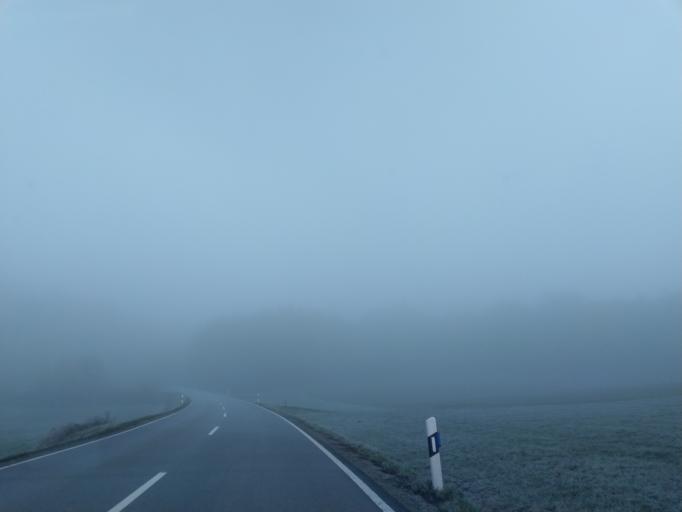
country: DE
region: Bavaria
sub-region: Lower Bavaria
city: Iggensbach
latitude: 48.7370
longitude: 13.1514
